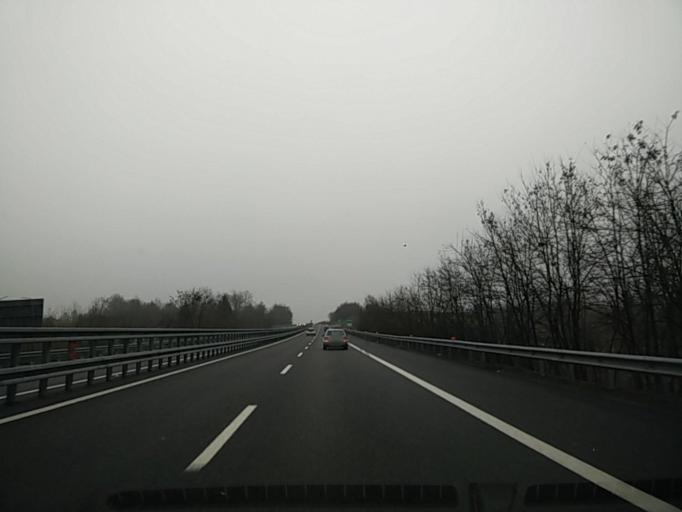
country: IT
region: Piedmont
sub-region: Provincia di Asti
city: Cerro Tanaro
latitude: 44.9044
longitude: 8.3685
